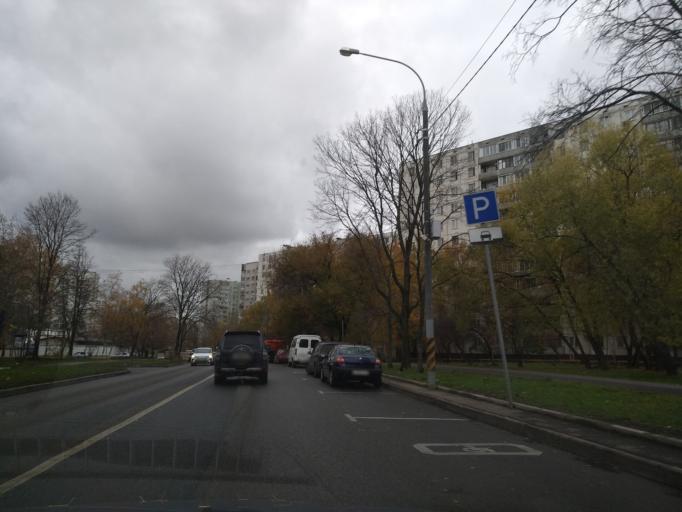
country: RU
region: Moscow
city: Bibirevo
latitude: 55.8879
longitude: 37.6003
